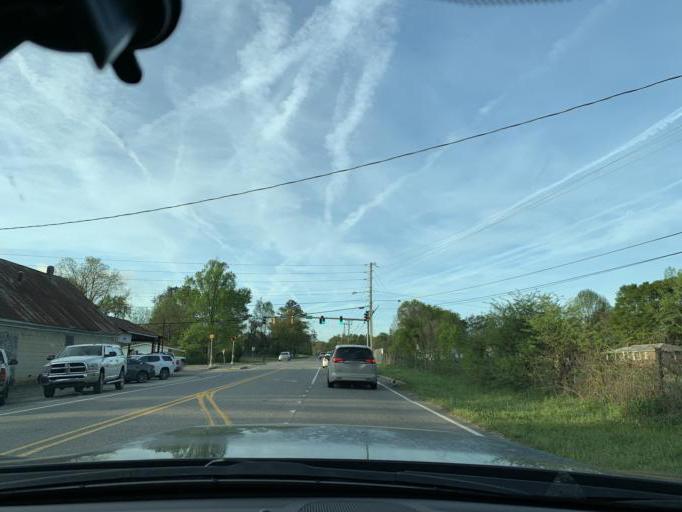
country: US
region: Georgia
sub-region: Forsyth County
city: Cumming
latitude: 34.2463
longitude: -84.1703
